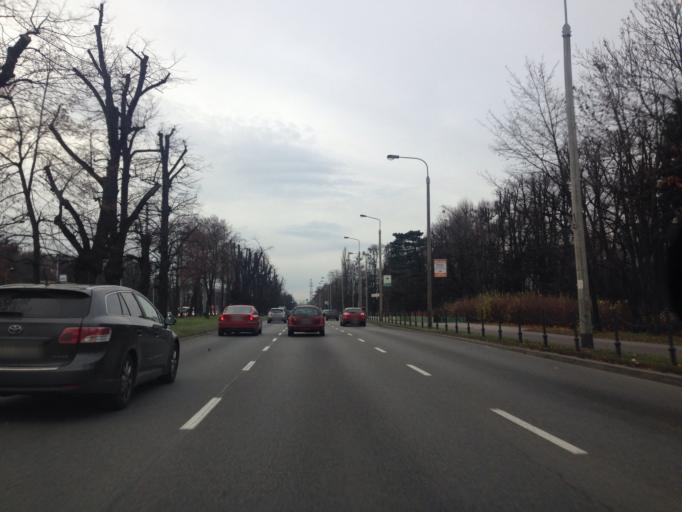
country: PL
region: Pomeranian Voivodeship
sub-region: Gdansk
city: Gdansk
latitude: 54.3666
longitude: 18.6344
